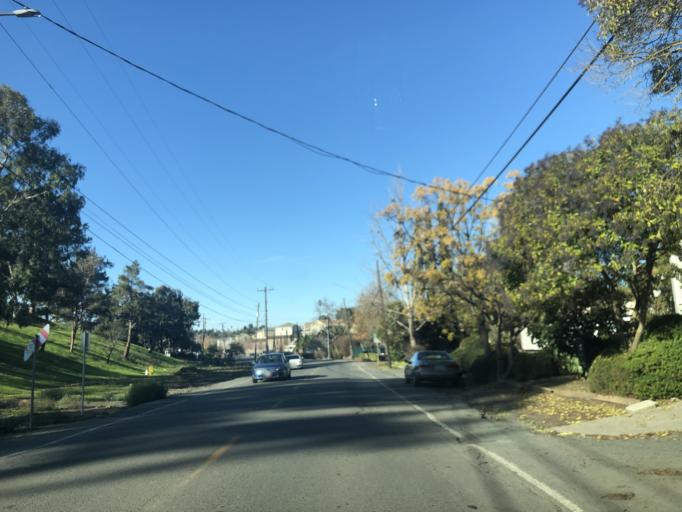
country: US
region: California
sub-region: Contra Costa County
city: Pacheco
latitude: 38.0004
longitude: -122.0796
